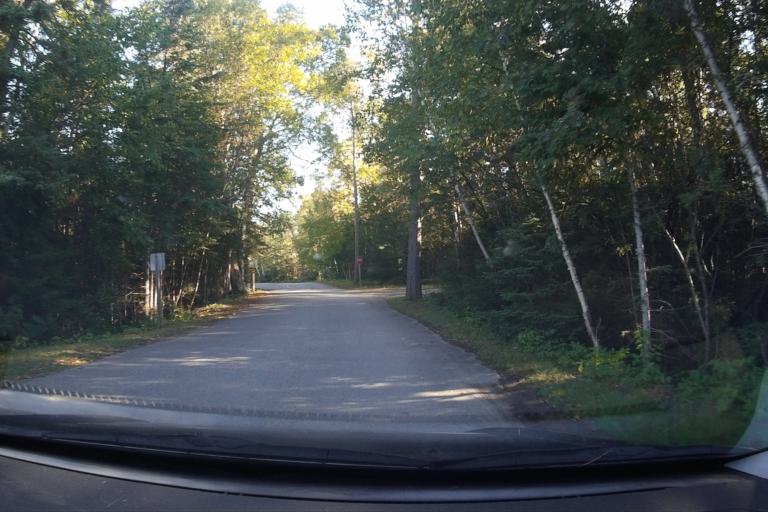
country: CA
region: Ontario
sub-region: Algoma
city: Sault Ste. Marie
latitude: 47.3339
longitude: -84.6153
